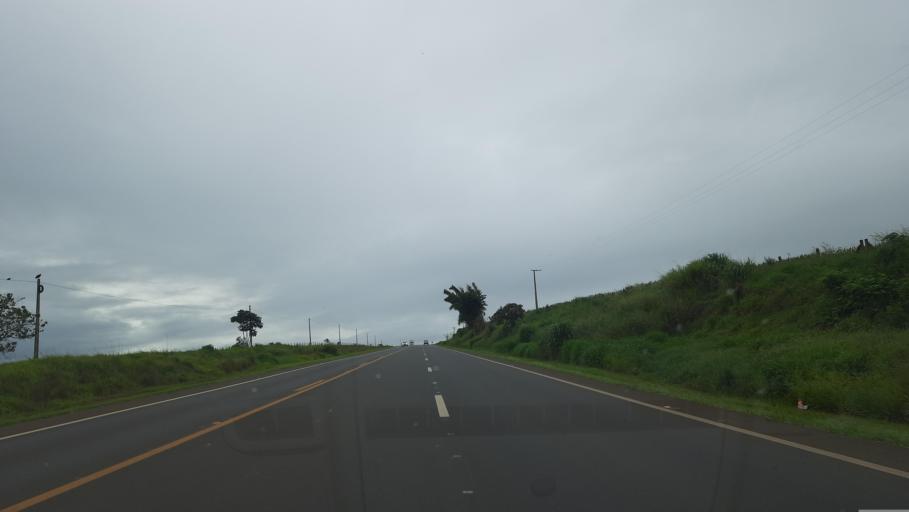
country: BR
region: Sao Paulo
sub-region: Casa Branca
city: Casa Branca
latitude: -21.7922
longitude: -47.0333
